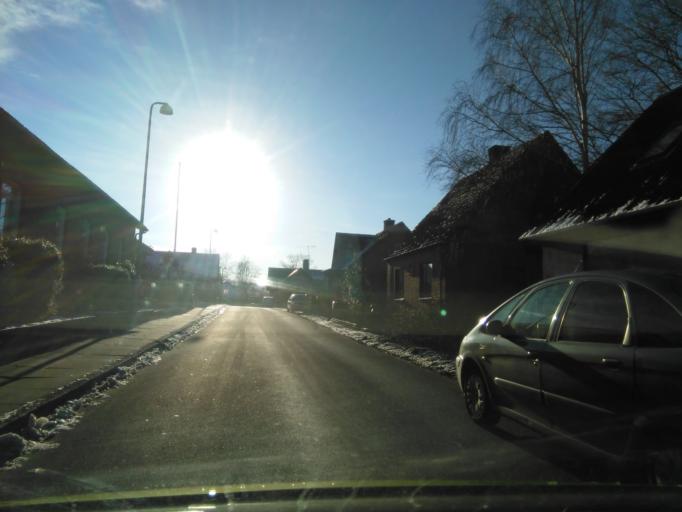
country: DK
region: Central Jutland
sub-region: Skanderborg Kommune
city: Skovby
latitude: 56.1179
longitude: 9.9563
